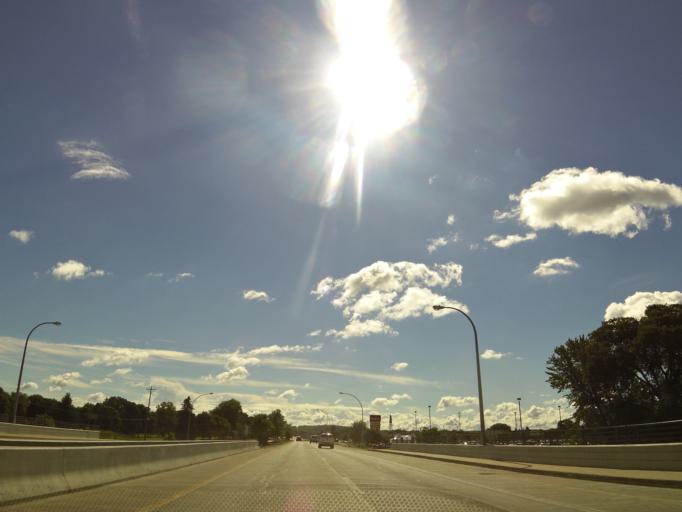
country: US
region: Minnesota
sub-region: Olmsted County
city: Rochester
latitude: 44.0069
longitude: -92.4720
